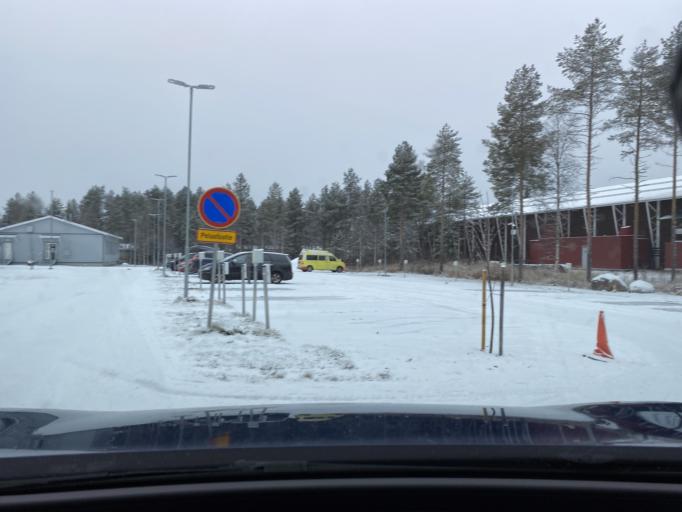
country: FI
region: Lapland
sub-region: Rovaniemi
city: Ranua
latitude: 65.9251
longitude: 26.5175
